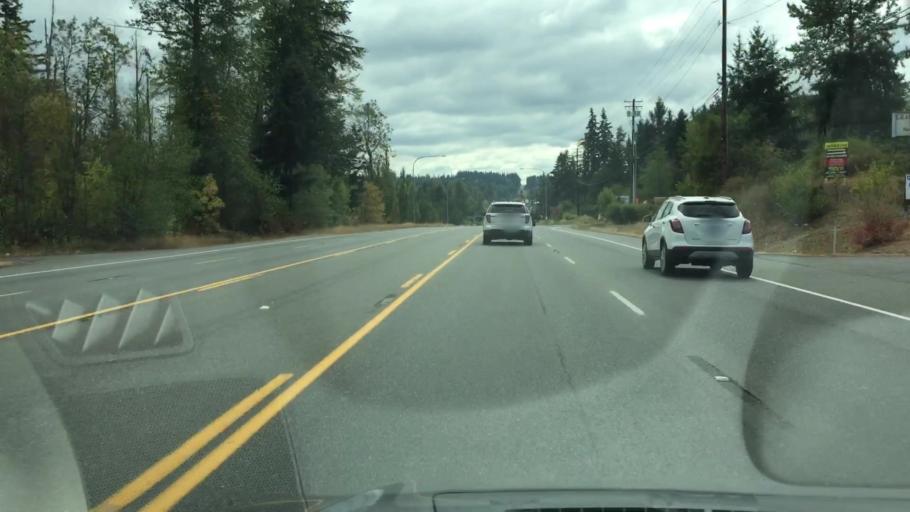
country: US
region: Washington
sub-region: Pierce County
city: Graham
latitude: 47.0646
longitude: -122.2948
